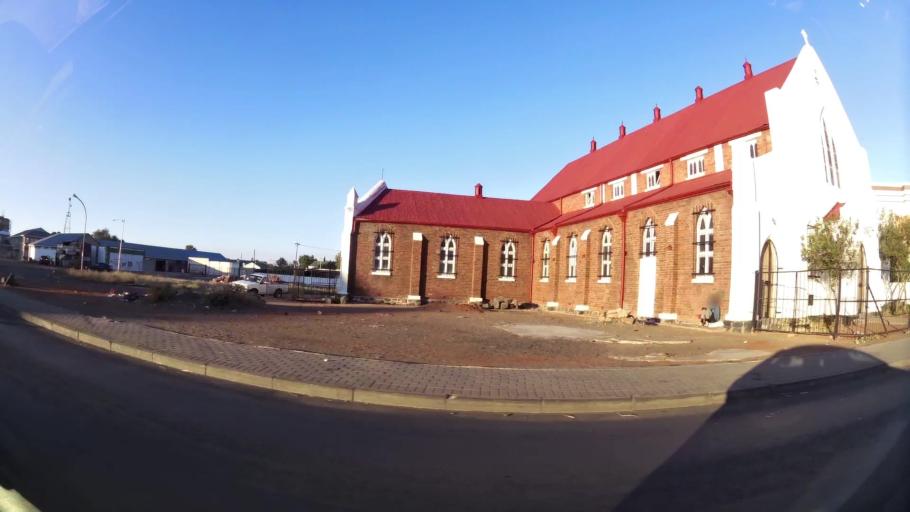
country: ZA
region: Northern Cape
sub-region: Frances Baard District Municipality
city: Kimberley
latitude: -28.7410
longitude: 24.7683
